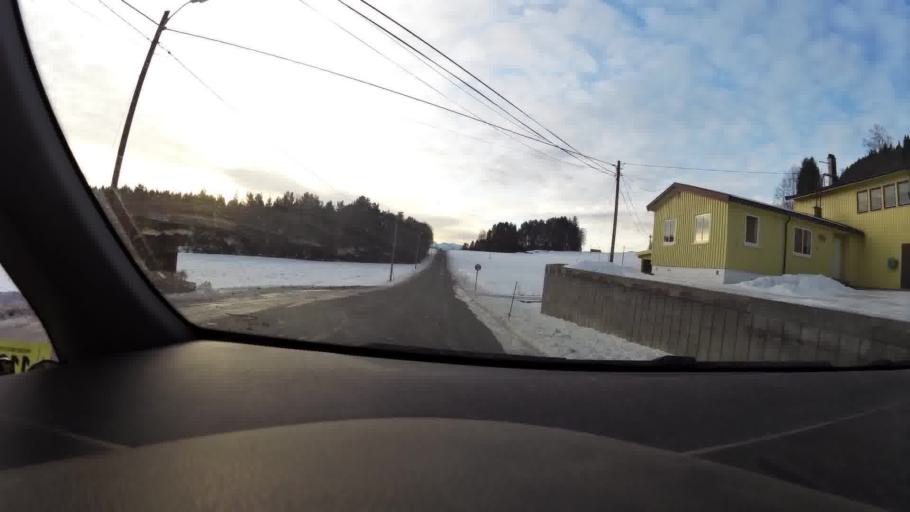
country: PL
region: Pomeranian Voivodeship
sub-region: Powiat wejherowski
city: Leczyce
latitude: 54.5767
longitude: 17.8449
